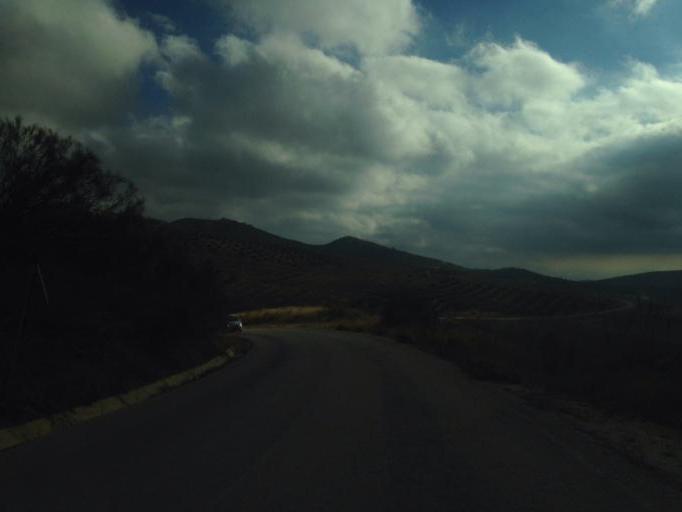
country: ES
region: Andalusia
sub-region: Provincia de Malaga
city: Colmenar
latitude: 36.9337
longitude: -4.3838
